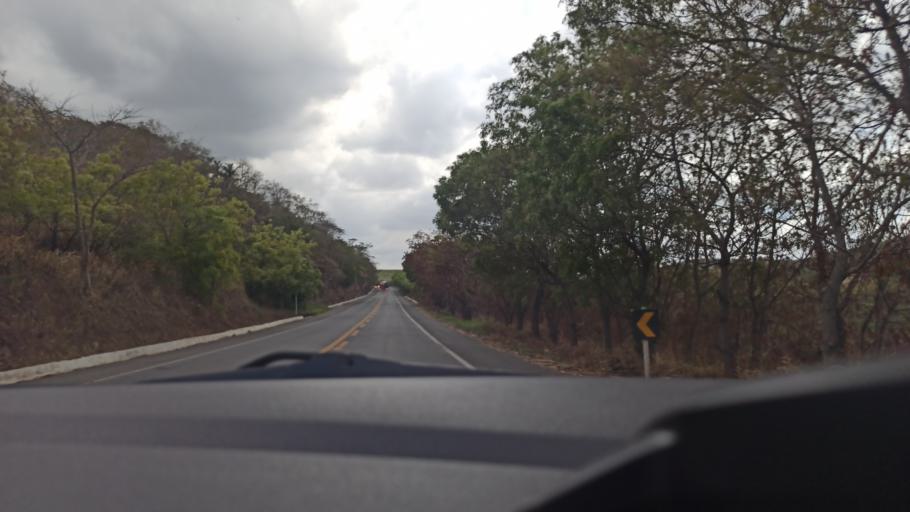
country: BR
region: Pernambuco
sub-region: Timbauba
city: Timbauba
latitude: -7.5396
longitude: -35.2827
